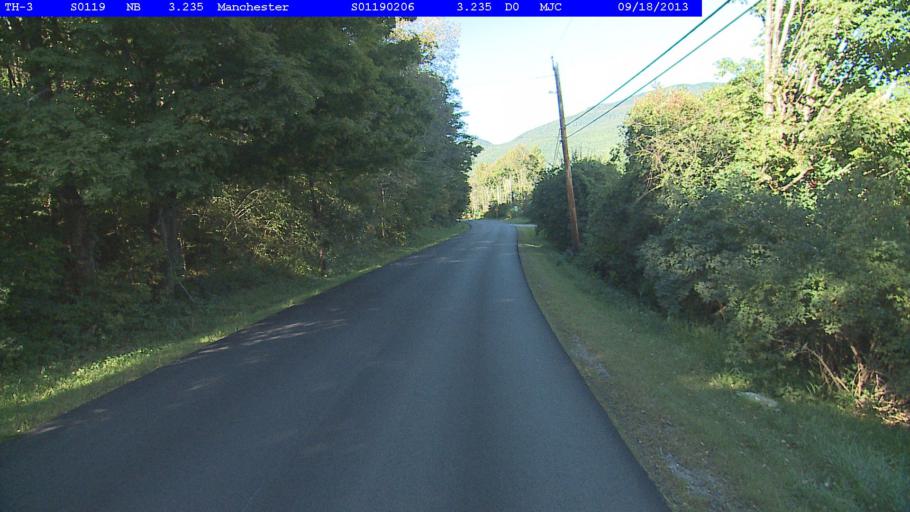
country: US
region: Vermont
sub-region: Bennington County
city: Manchester Center
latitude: 43.2096
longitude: -73.0678
